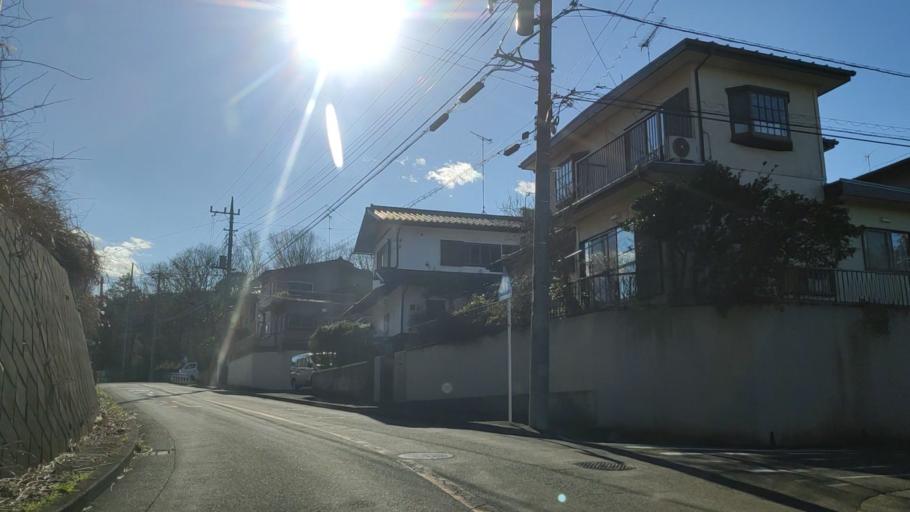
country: JP
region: Kanagawa
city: Minami-rinkan
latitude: 35.5049
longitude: 139.5272
